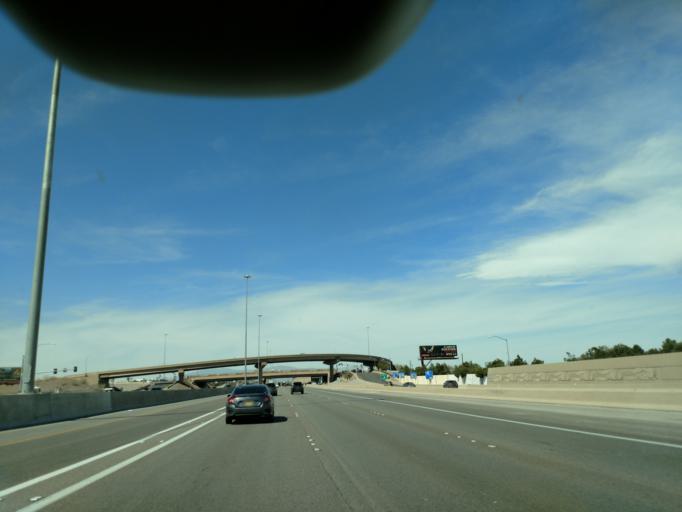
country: US
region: Nevada
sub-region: Clark County
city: Enterprise
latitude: 36.0397
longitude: -115.1807
